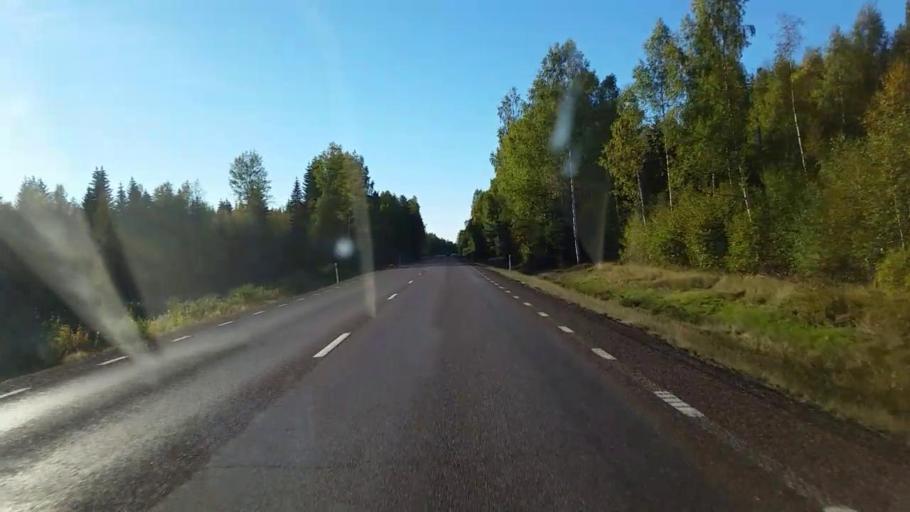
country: SE
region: Gaevleborg
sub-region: Ljusdals Kommun
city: Jaervsoe
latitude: 61.8093
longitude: 16.2256
